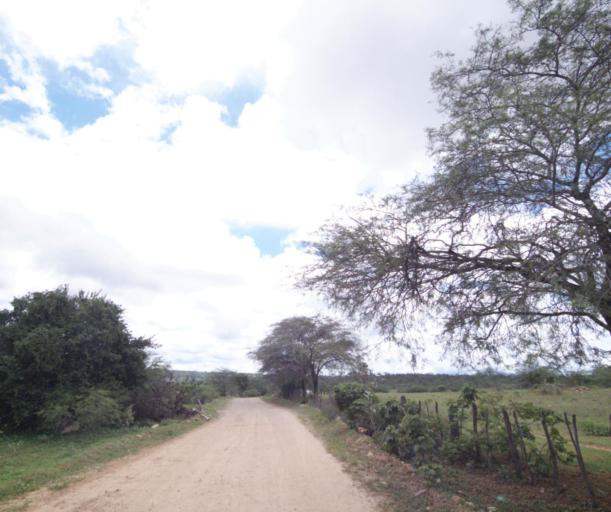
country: BR
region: Bahia
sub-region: Tanhacu
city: Tanhacu
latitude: -14.1658
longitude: -41.1610
